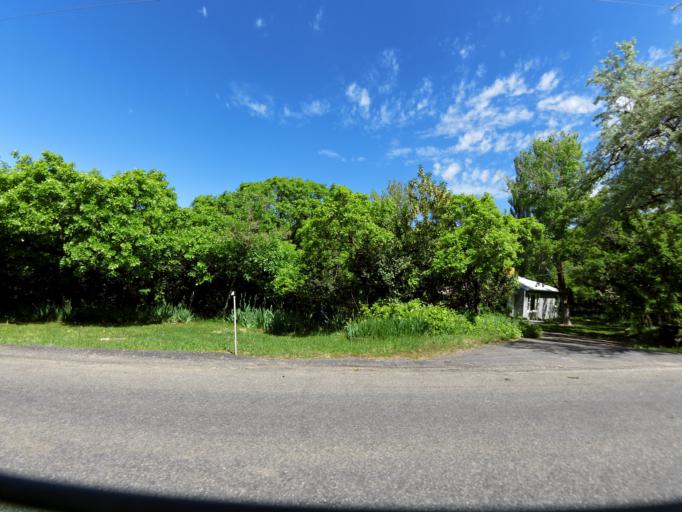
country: US
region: Utah
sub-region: Weber County
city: Uintah
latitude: 41.1786
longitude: -111.9356
